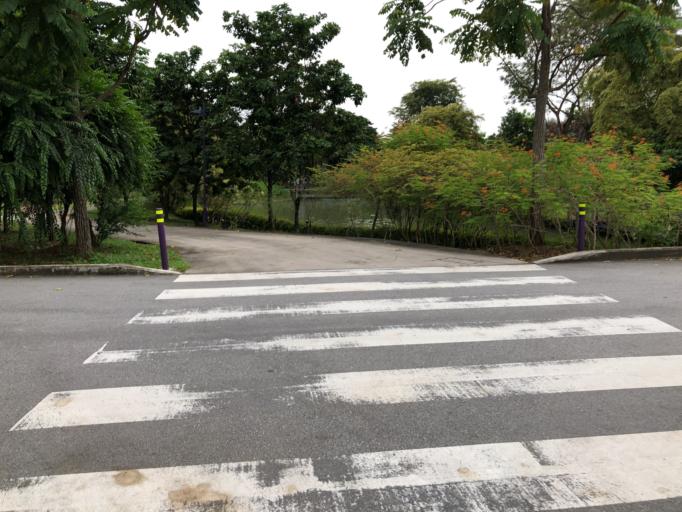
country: SG
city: Singapore
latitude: 1.2783
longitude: 103.8603
